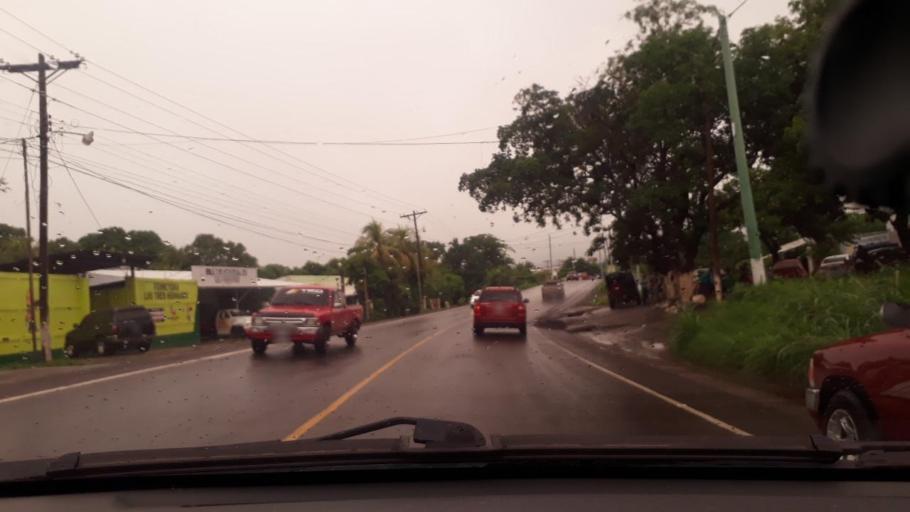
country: SV
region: Ahuachapan
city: San Francisco Menendez
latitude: 13.8756
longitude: -90.0971
